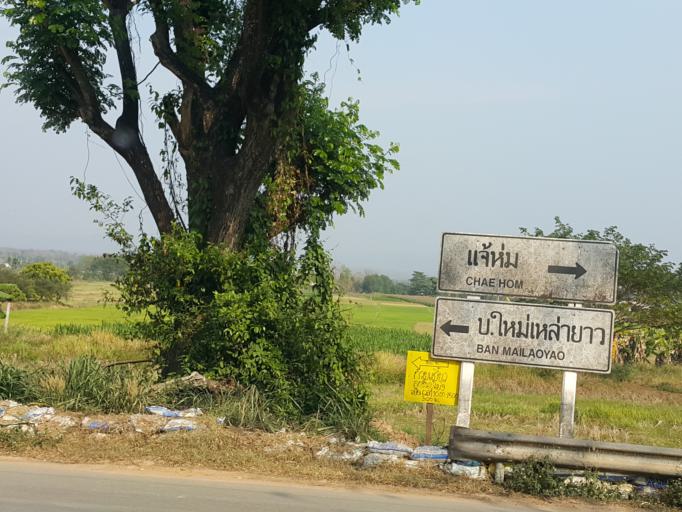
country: TH
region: Lampang
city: Chae Hom
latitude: 18.7238
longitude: 99.5617
